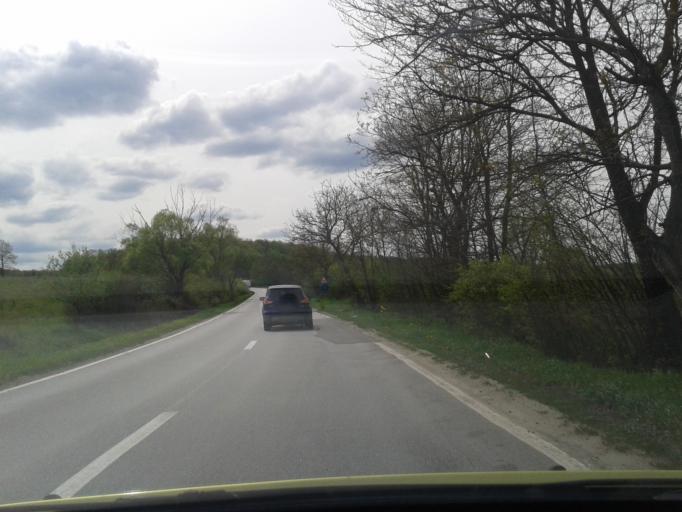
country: RO
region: Hunedoara
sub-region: Comuna Dobra
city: Dobra
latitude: 45.9175
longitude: 22.5523
